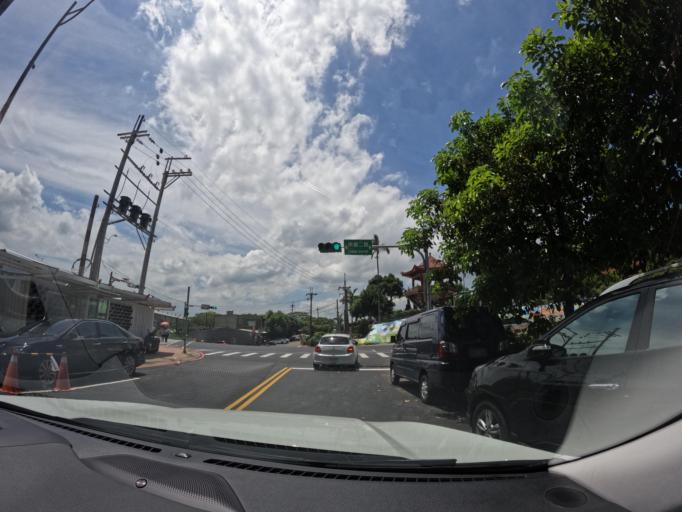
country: TW
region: Taiwan
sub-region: Taoyuan
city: Taoyuan
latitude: 25.0474
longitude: 121.3826
